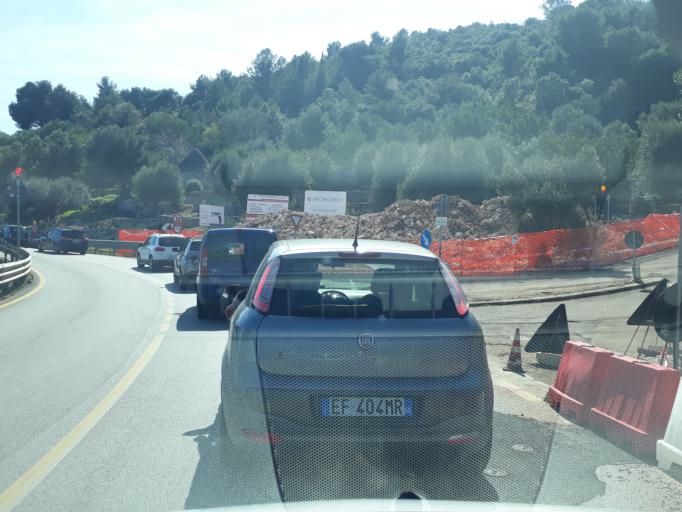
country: IT
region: Apulia
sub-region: Provincia di Brindisi
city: Lamie di Olimpie-Selva
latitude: 40.8161
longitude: 17.3447
